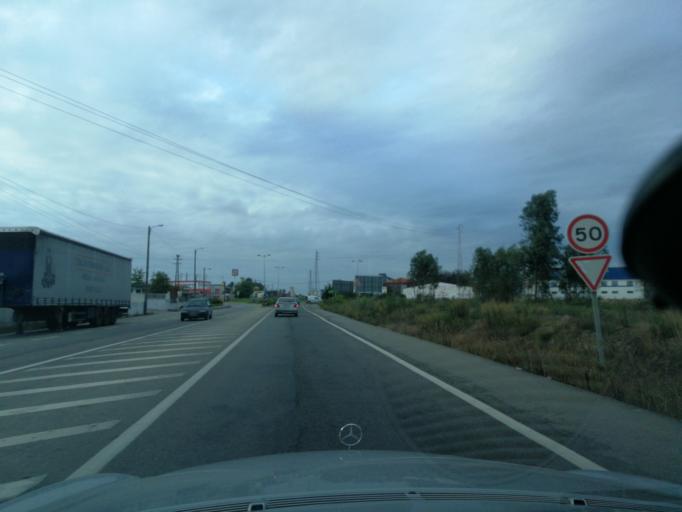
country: PT
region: Aveiro
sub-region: Agueda
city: Agueda
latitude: 40.5935
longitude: -8.4560
